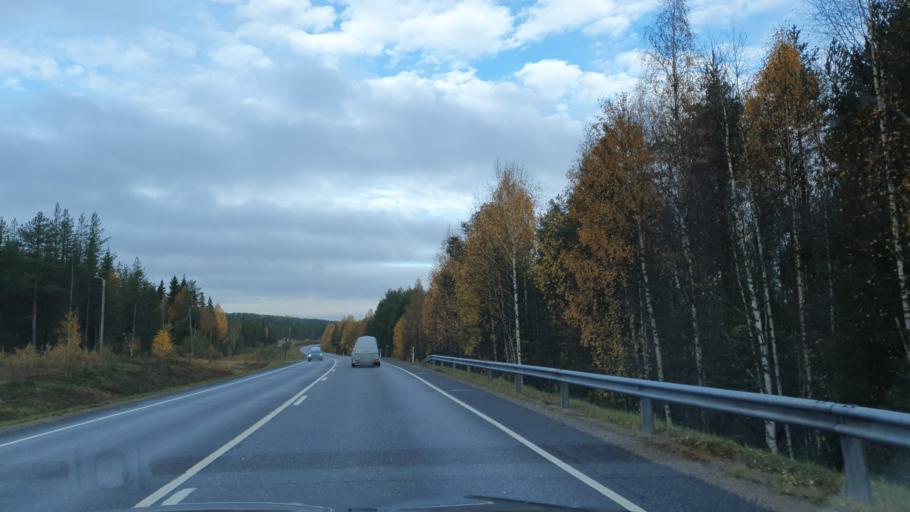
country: FI
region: Lapland
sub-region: Rovaniemi
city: Rovaniemi
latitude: 66.5911
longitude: 25.6080
